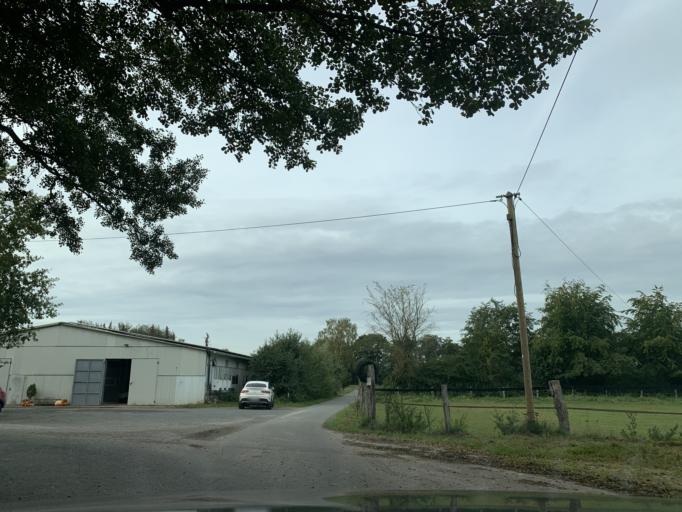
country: DE
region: North Rhine-Westphalia
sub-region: Regierungsbezirk Dusseldorf
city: Hunxe
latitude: 51.6826
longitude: 6.8092
